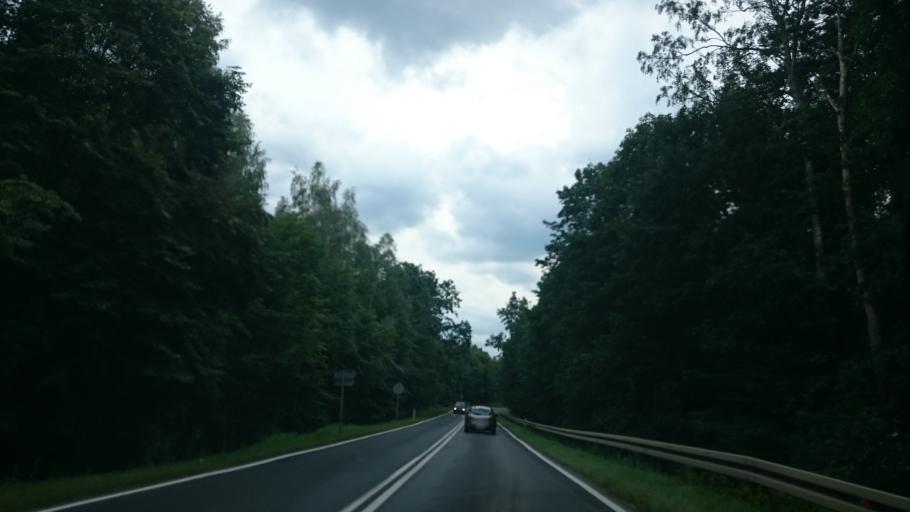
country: PL
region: Kujawsko-Pomorskie
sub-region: Powiat tucholski
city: Tuchola
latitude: 53.5613
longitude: 17.9011
